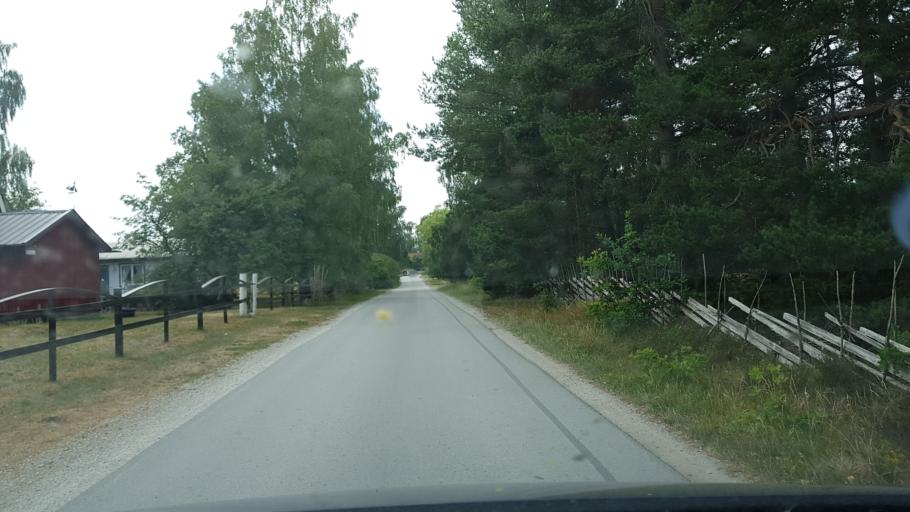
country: SE
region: Gotland
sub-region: Gotland
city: Hemse
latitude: 57.3370
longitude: 18.7063
